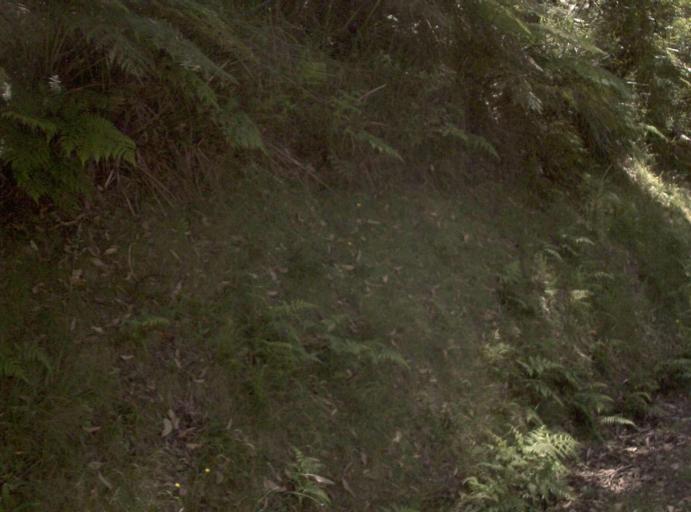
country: AU
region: Victoria
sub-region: Yarra Ranges
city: Millgrove
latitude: -37.7371
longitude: 145.7214
